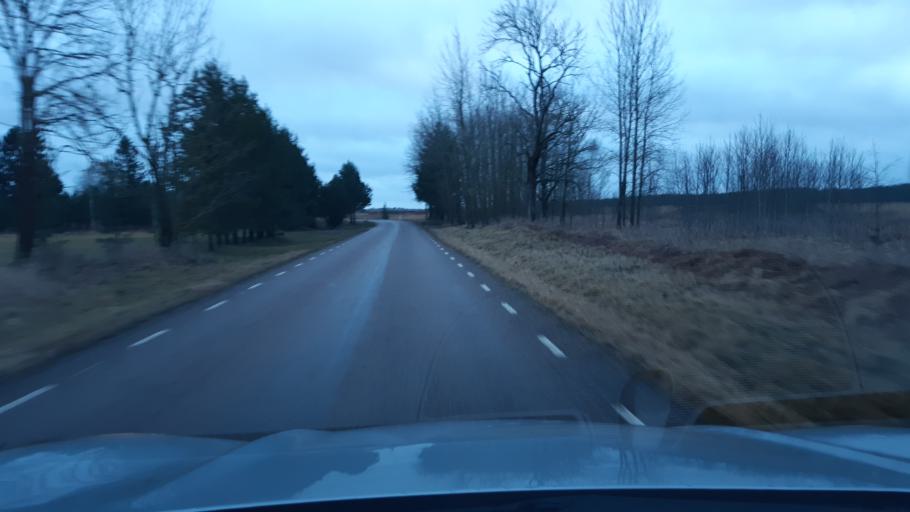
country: EE
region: Raplamaa
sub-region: Rapla vald
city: Rapla
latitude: 59.0005
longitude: 24.7166
